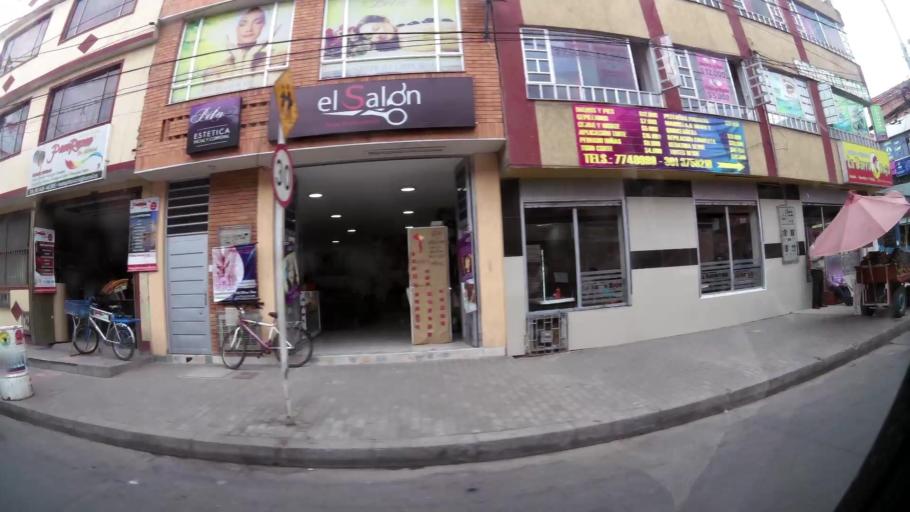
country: CO
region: Cundinamarca
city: Funza
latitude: 4.7113
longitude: -74.1402
